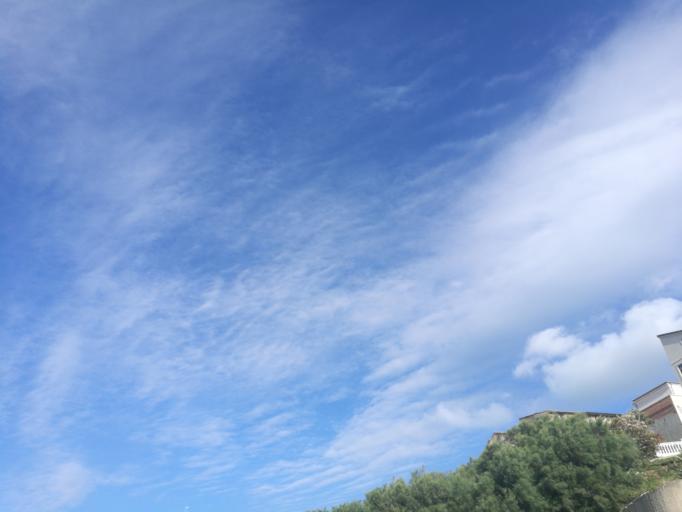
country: IT
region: Molise
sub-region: Provincia di Campobasso
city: Termoli
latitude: 42.0040
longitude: 14.9933
